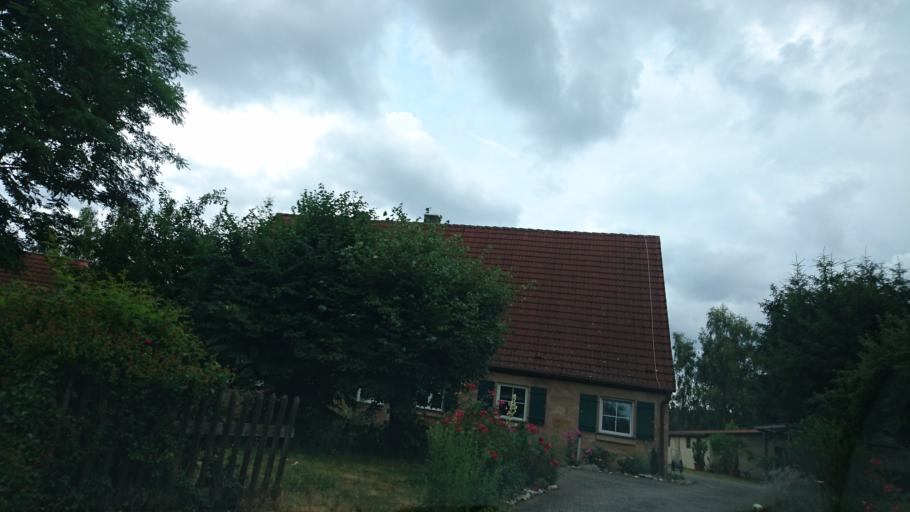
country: DE
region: Bavaria
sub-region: Regierungsbezirk Mittelfranken
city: Heideck
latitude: 49.1893
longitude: 11.1070
